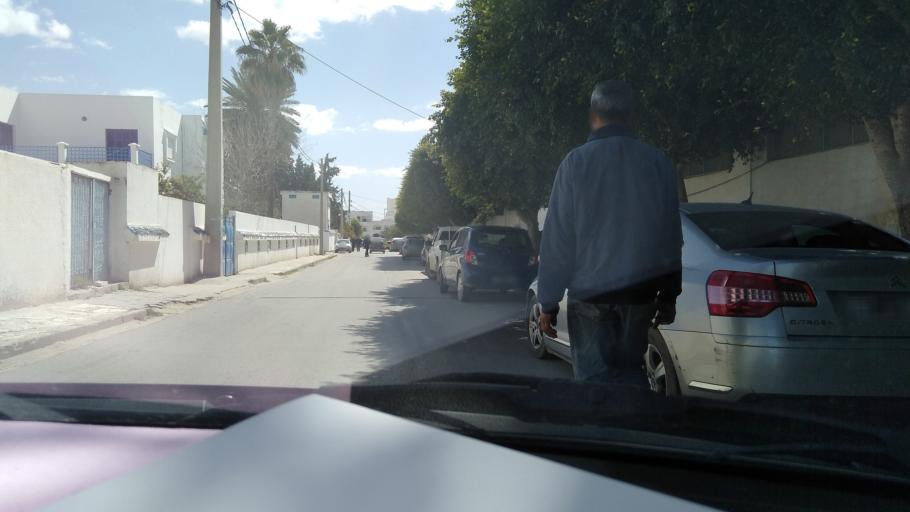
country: TN
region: Al Qayrawan
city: Kairouan
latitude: 35.6702
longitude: 10.1065
